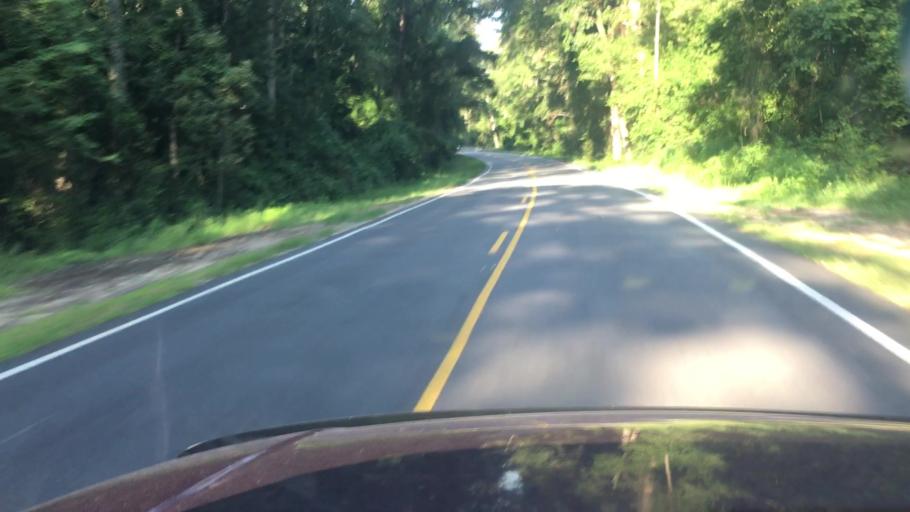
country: US
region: North Carolina
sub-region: Robeson County
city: Saint Pauls
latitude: 34.8332
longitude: -78.9018
